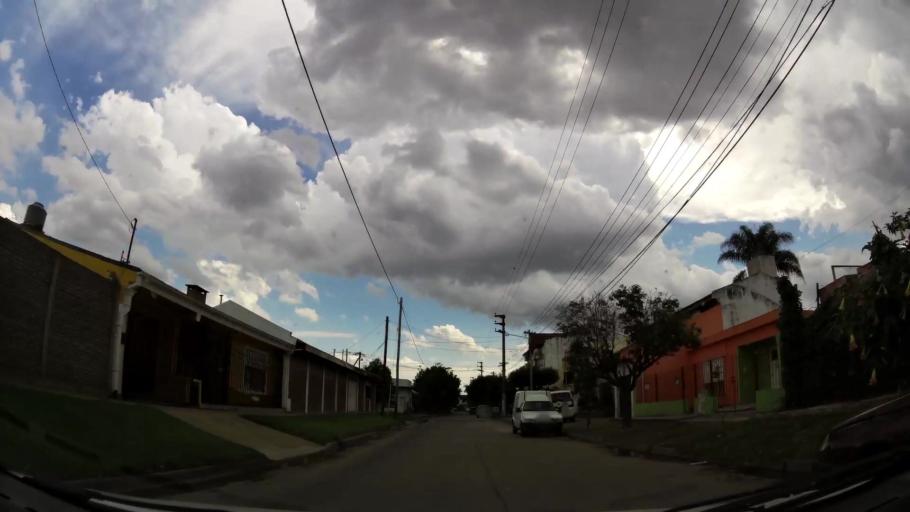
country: AR
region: Buenos Aires
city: Ituzaingo
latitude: -34.6439
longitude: -58.6812
